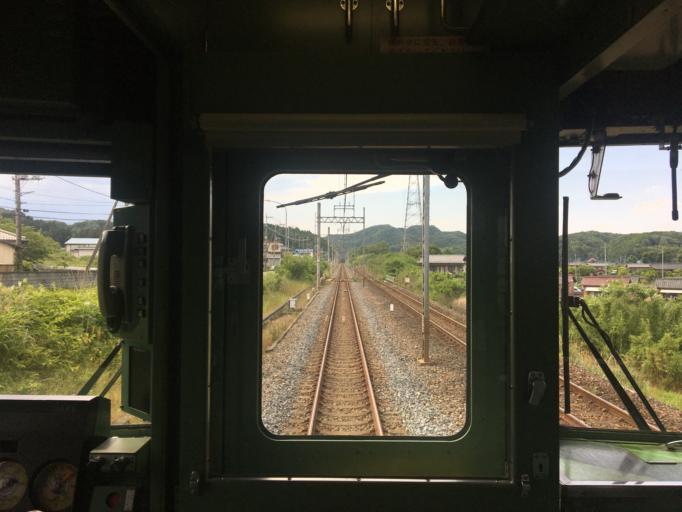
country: JP
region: Saitama
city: Ogawa
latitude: 36.0660
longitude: 139.2460
